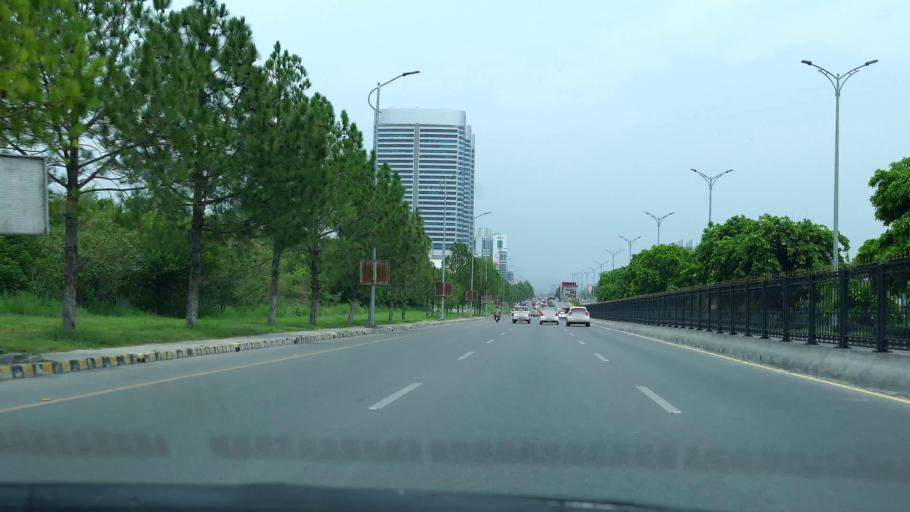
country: PK
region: Islamabad
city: Islamabad
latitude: 33.7009
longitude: 73.0387
